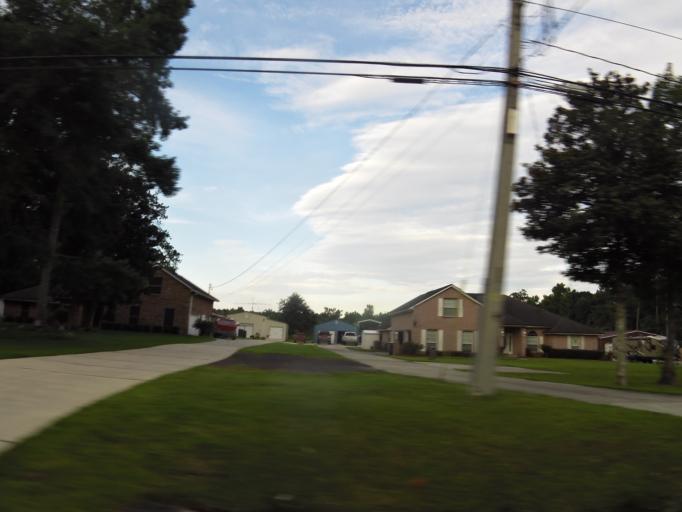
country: US
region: Florida
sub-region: Nassau County
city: Nassau Village-Ratliff
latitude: 30.3650
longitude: -81.8069
